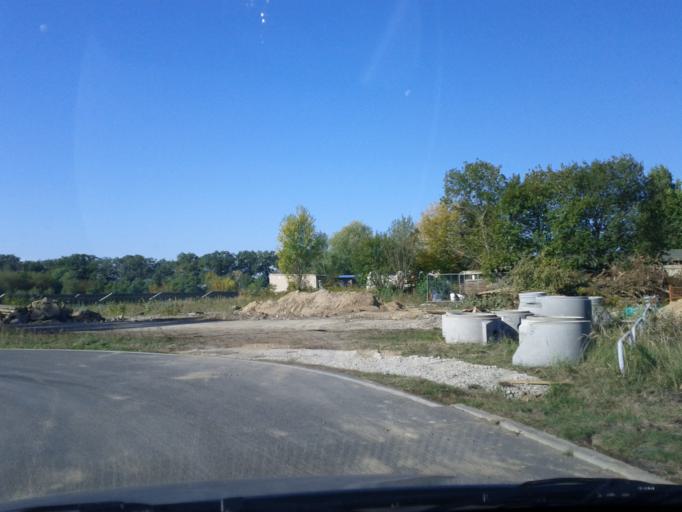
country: DE
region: Brandenburg
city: Schoneiche
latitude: 52.4899
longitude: 13.6996
